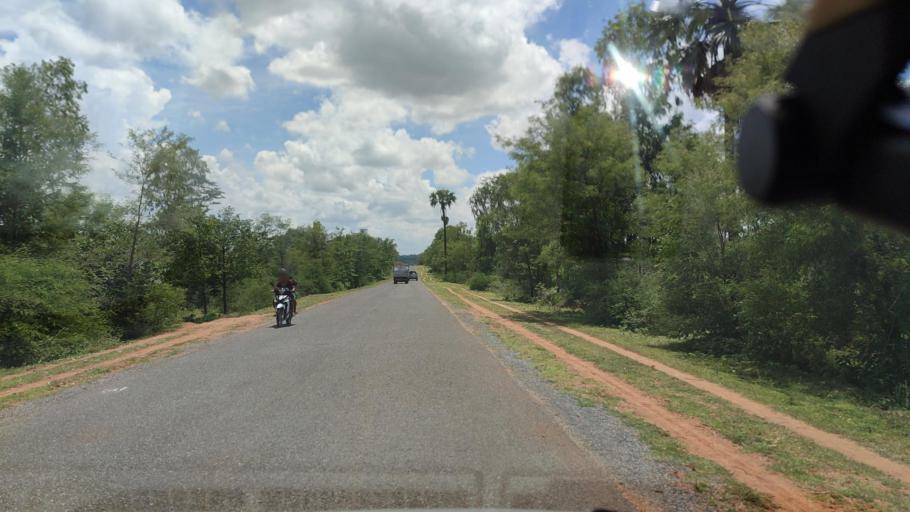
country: MM
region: Magway
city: Magway
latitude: 20.1923
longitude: 95.1531
